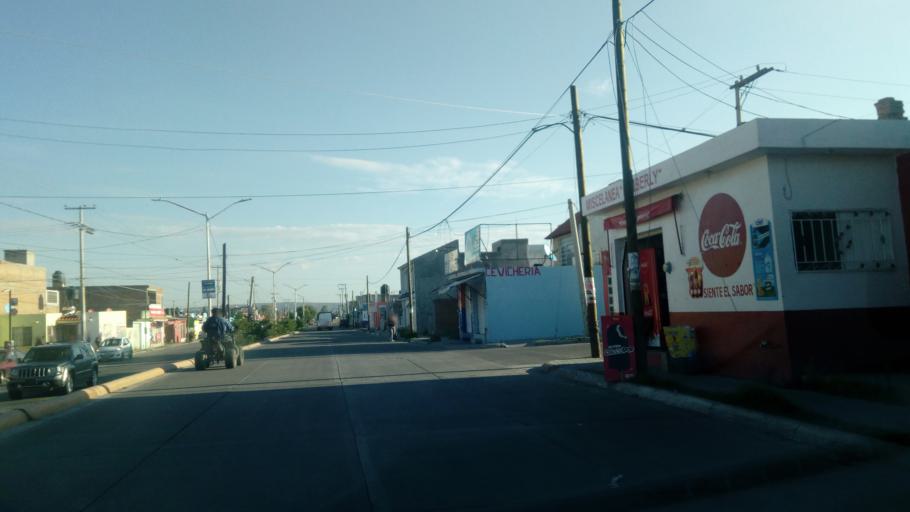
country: MX
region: Durango
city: Victoria de Durango
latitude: 24.0623
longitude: -104.5852
